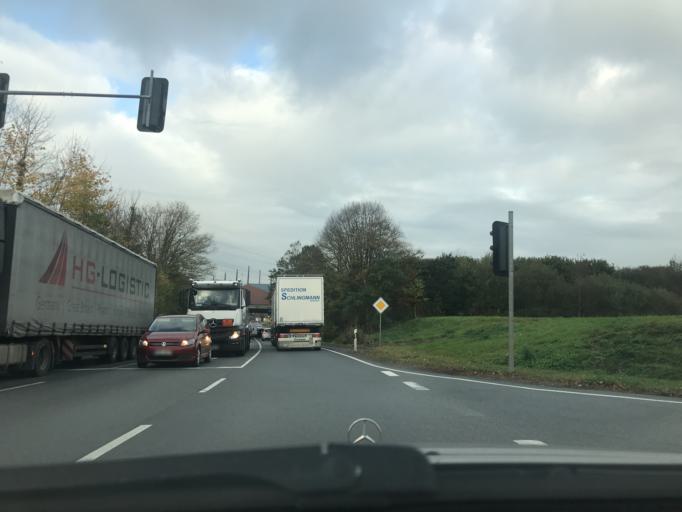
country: DE
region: North Rhine-Westphalia
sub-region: Regierungsbezirk Arnsberg
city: Welver
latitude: 51.6943
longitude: 7.9709
